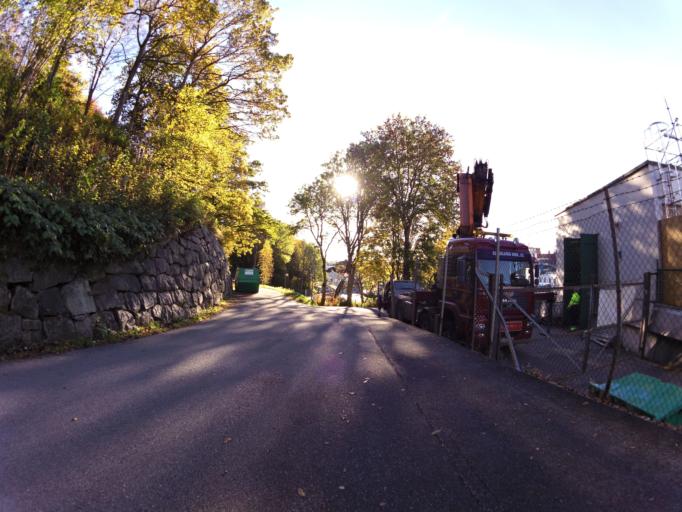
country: NO
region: Ostfold
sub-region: Sarpsborg
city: Sarpsborg
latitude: 59.2751
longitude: 11.1310
